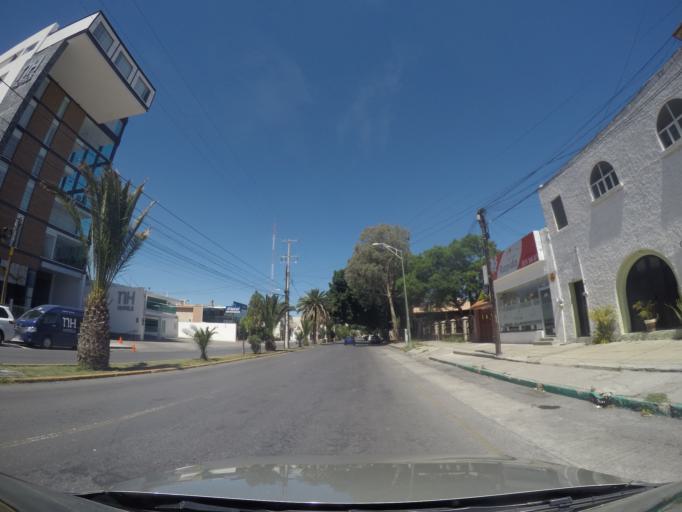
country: MX
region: San Luis Potosi
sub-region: San Luis Potosi
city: San Luis Potosi
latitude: 22.1498
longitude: -100.9962
